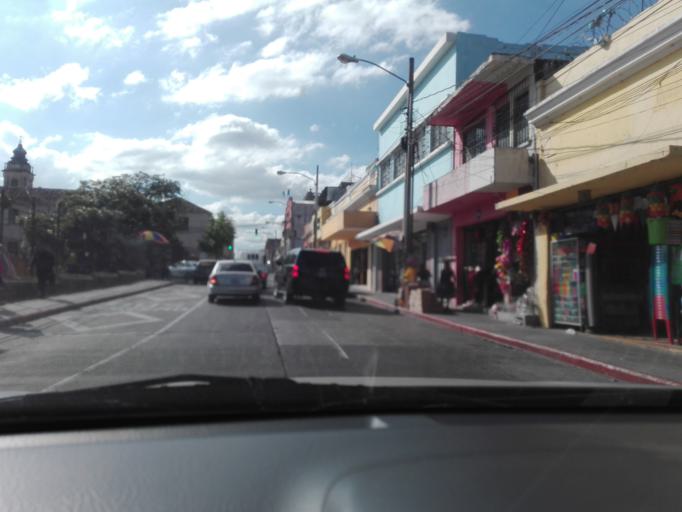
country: GT
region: Guatemala
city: Guatemala City
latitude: 14.6421
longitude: -90.5109
